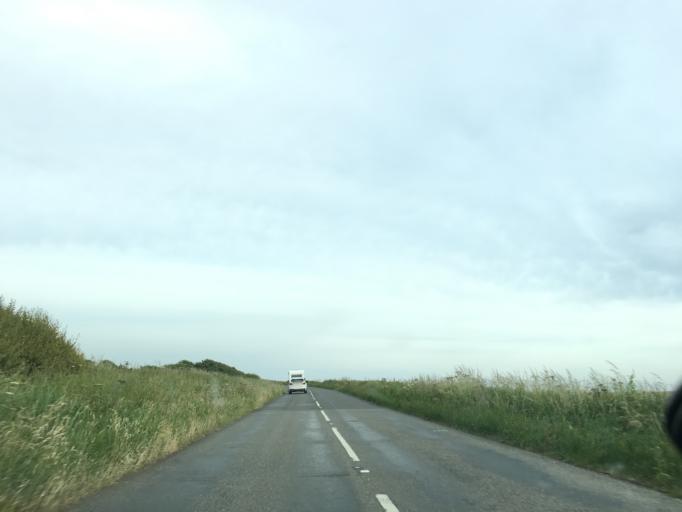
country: GB
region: England
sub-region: Isle of Wight
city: Shalfleet
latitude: 50.6406
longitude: -1.4272
